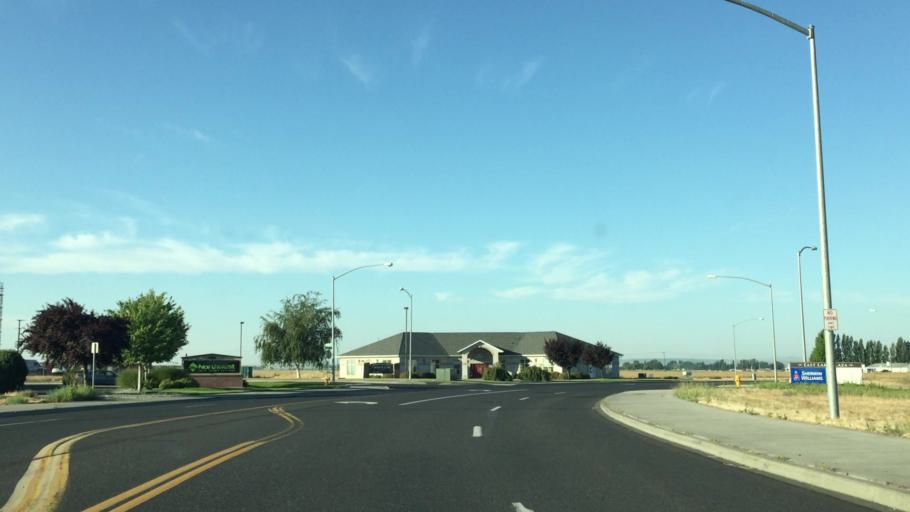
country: US
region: Washington
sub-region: Grant County
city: Moses Lake
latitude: 47.1048
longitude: -119.2533
